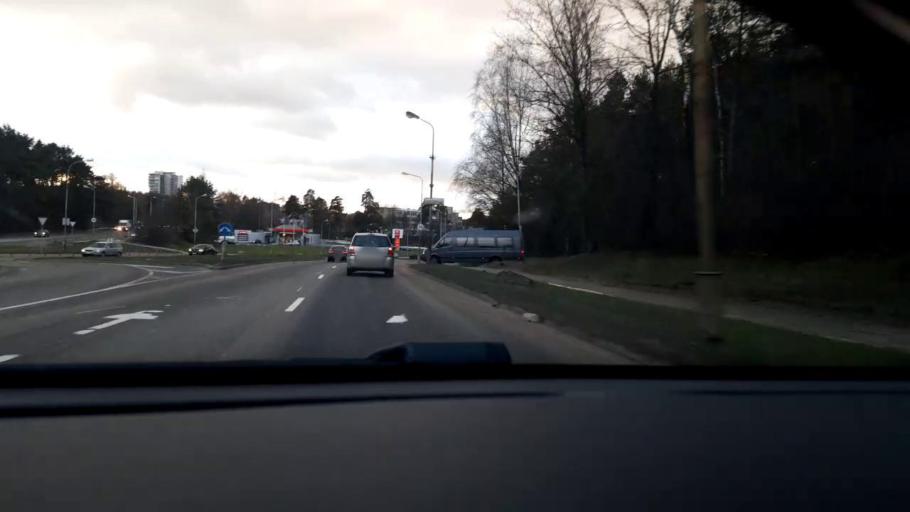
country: LT
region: Vilnius County
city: Rasos
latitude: 54.7299
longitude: 25.3301
